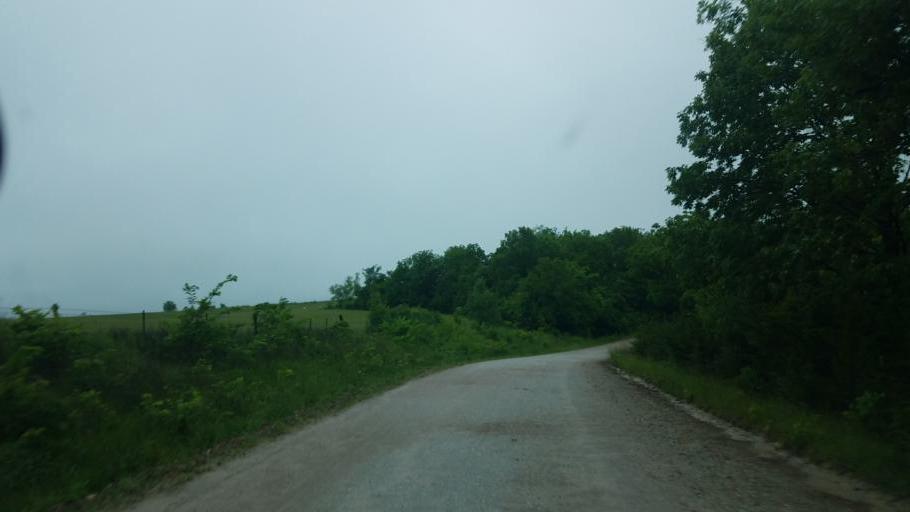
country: US
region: Missouri
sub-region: Moniteau County
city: California
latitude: 38.7575
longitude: -92.6066
